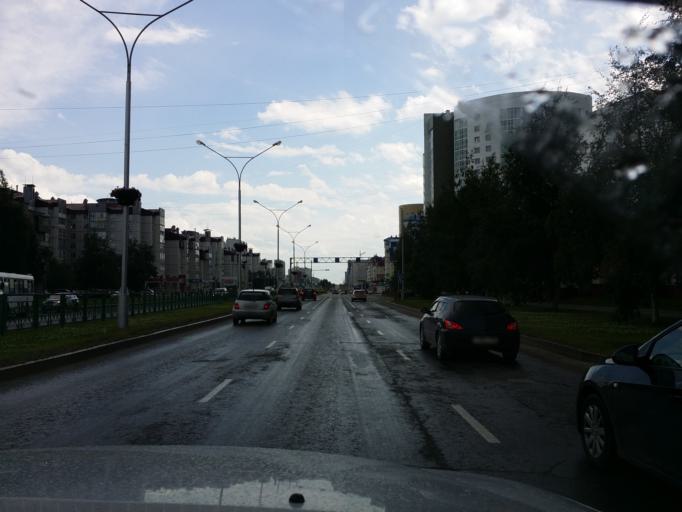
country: RU
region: Khanty-Mansiyskiy Avtonomnyy Okrug
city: Nizhnevartovsk
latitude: 60.9388
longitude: 76.5735
